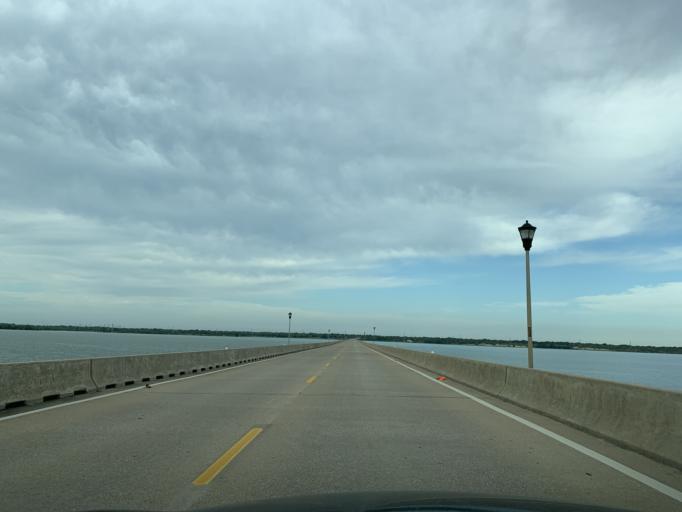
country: US
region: Texas
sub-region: Dallas County
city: Grand Prairie
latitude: 32.7079
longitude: -96.9565
